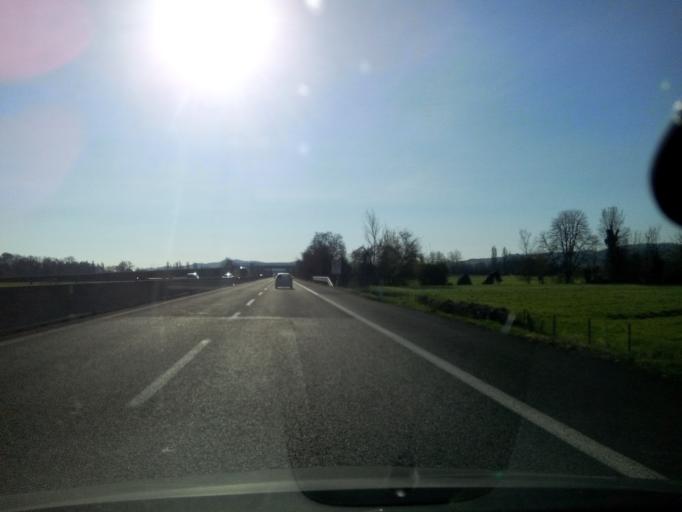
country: IT
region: Emilia-Romagna
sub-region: Provincia di Bologna
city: Zola Predosa
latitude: 44.5034
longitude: 11.2117
